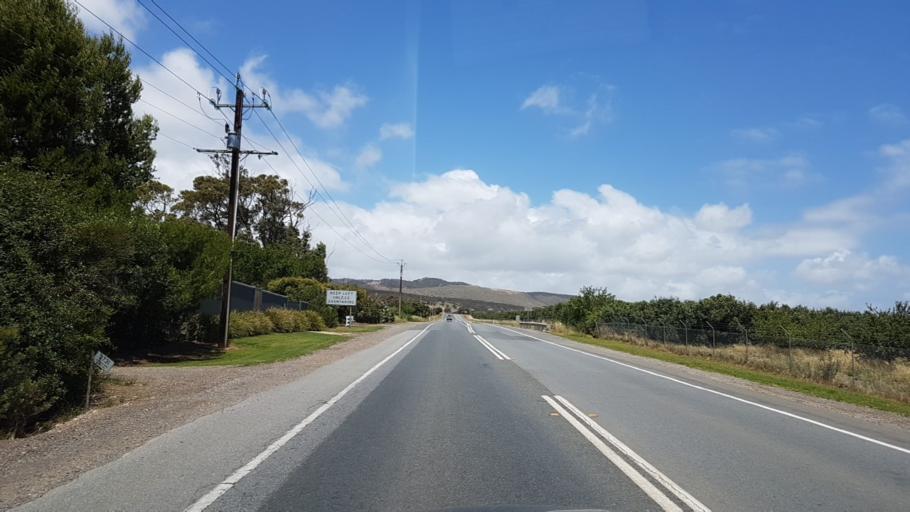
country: AU
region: South Australia
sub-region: Onkaparinga
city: Aldinga
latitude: -35.3126
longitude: 138.4736
